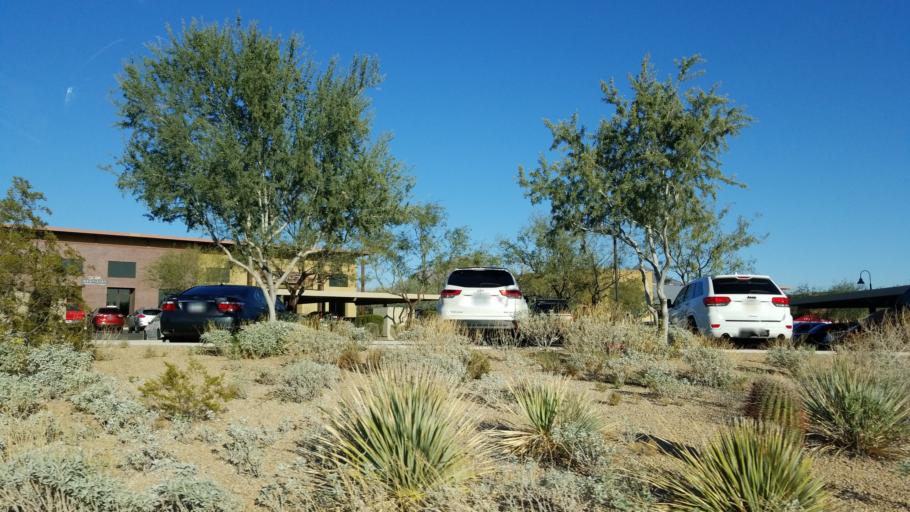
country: US
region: Arizona
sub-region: Maricopa County
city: Paradise Valley
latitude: 33.6579
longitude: -111.8906
